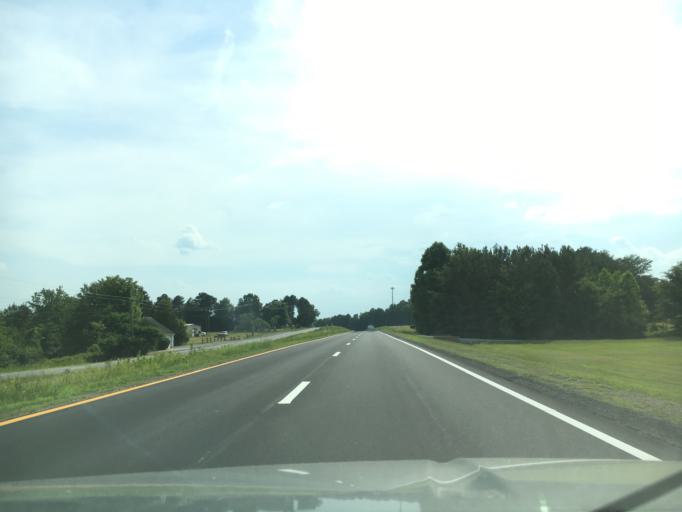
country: US
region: Virginia
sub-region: Halifax County
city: Halifax
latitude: 36.8038
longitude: -78.7687
